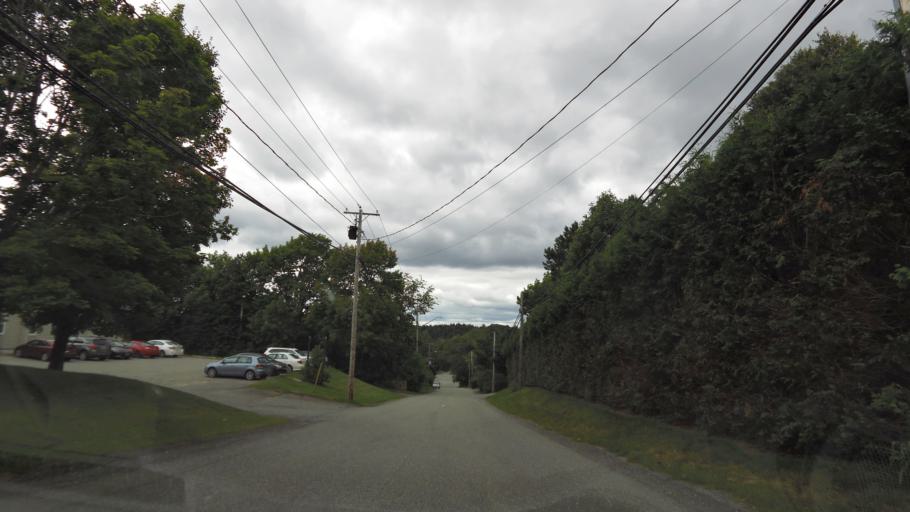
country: CA
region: New Brunswick
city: Hampton
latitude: 45.5236
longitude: -65.8255
